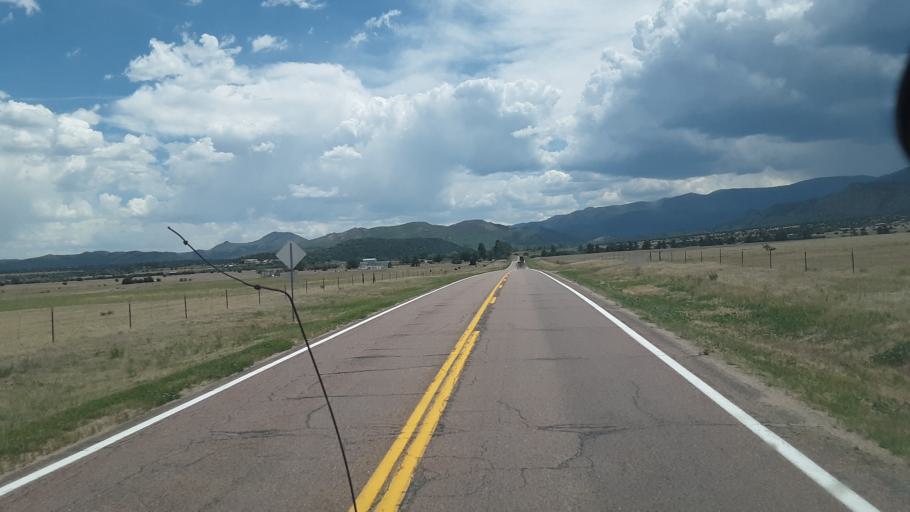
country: US
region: Colorado
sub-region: Fremont County
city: Florence
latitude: 38.2536
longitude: -105.0903
